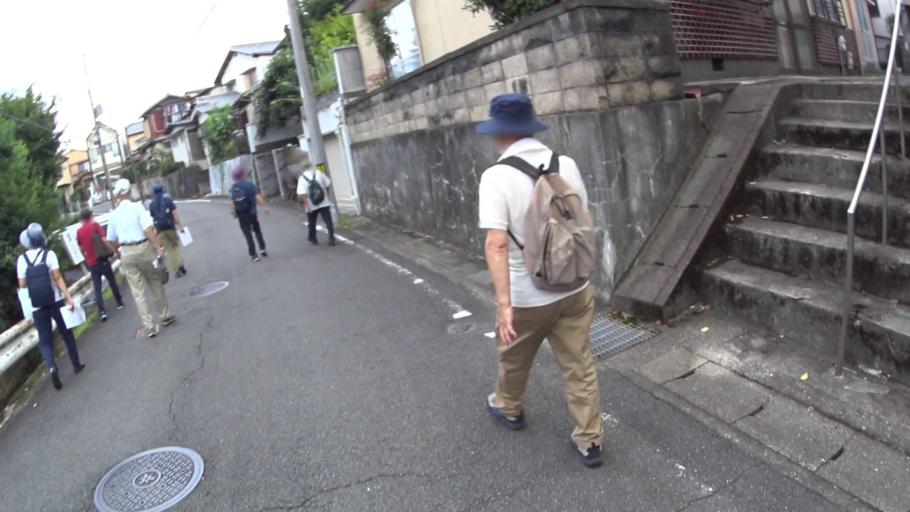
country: JP
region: Kyoto
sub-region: Kyoto-shi
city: Kamigyo-ku
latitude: 35.0428
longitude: 135.7352
